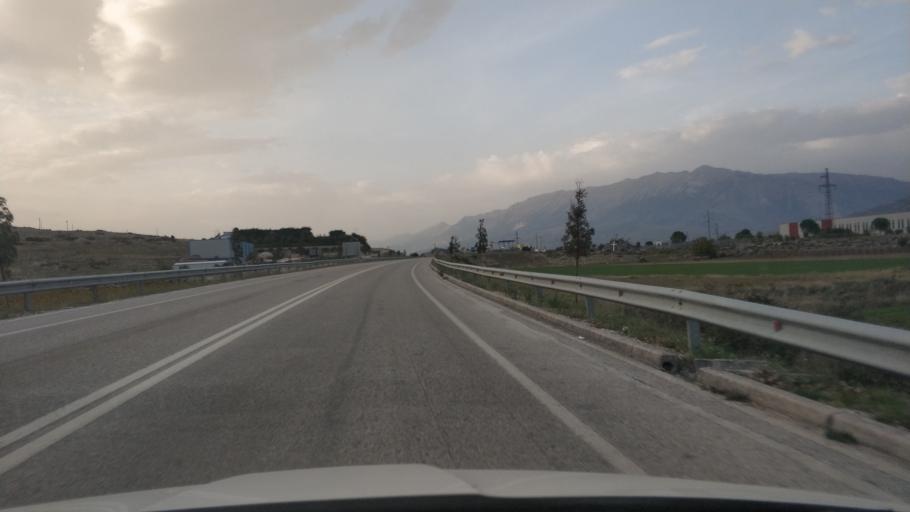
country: AL
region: Gjirokaster
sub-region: Rrethi i Gjirokastres
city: Libohove
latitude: 39.9707
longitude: 20.2367
